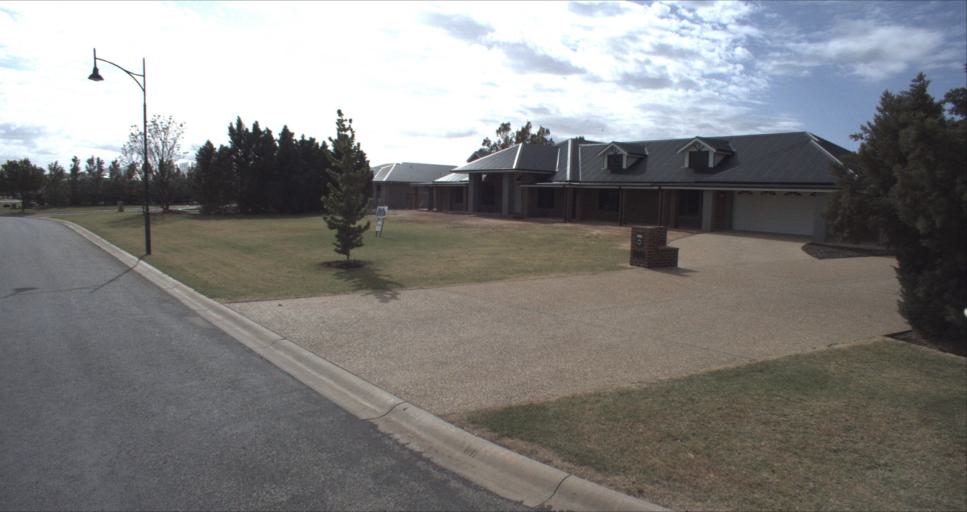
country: AU
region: New South Wales
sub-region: Leeton
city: Leeton
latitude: -34.5606
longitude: 146.4277
